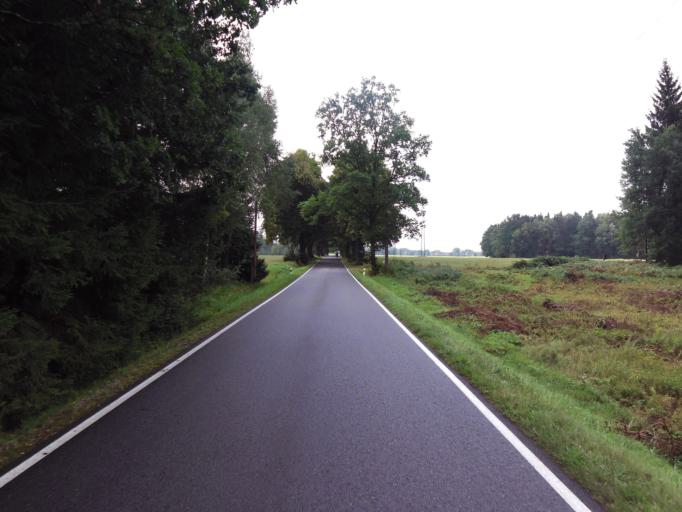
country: CZ
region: Jihocesky
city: Chlum u Trebone
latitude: 48.9181
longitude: 14.9202
